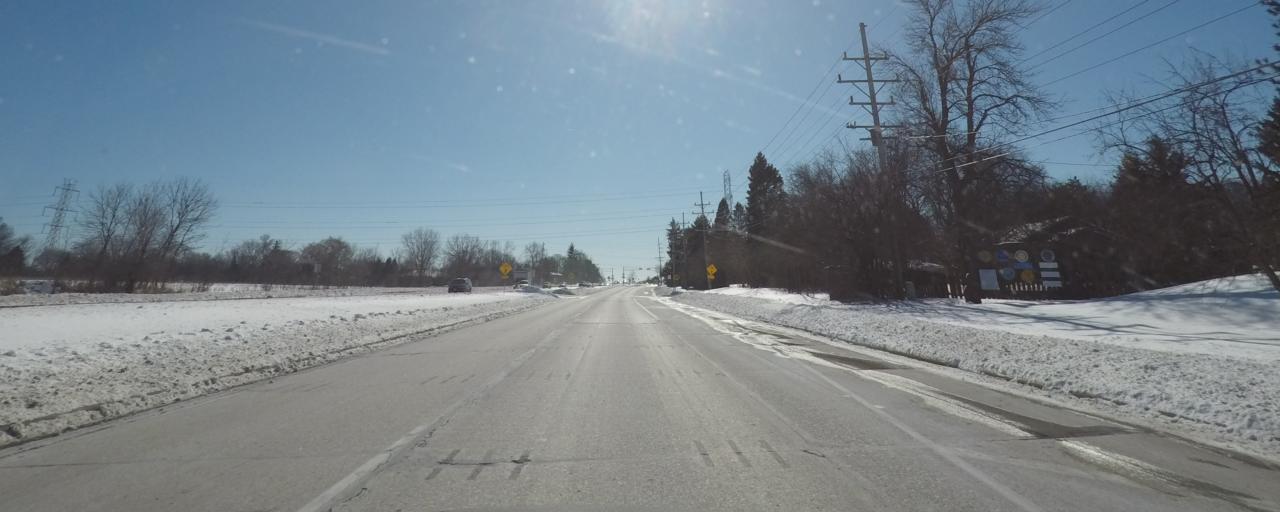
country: US
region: Wisconsin
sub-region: Waukesha County
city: New Berlin
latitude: 43.0122
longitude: -88.1075
